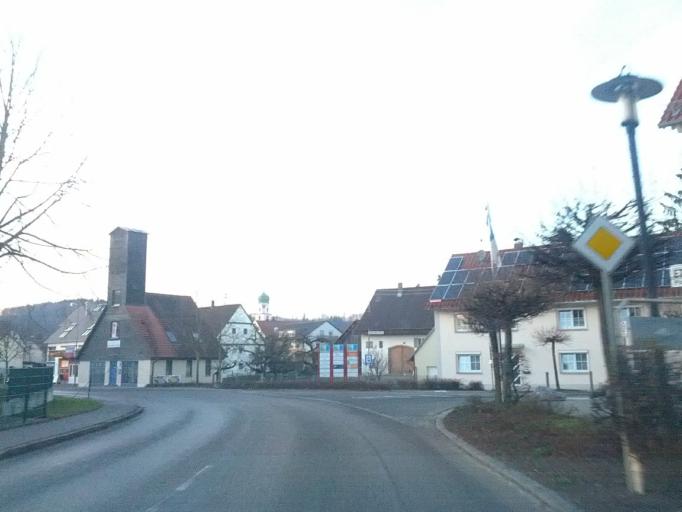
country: DE
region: Baden-Wuerttemberg
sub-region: Tuebingen Region
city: Aitrach
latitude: 47.9392
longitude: 10.0919
